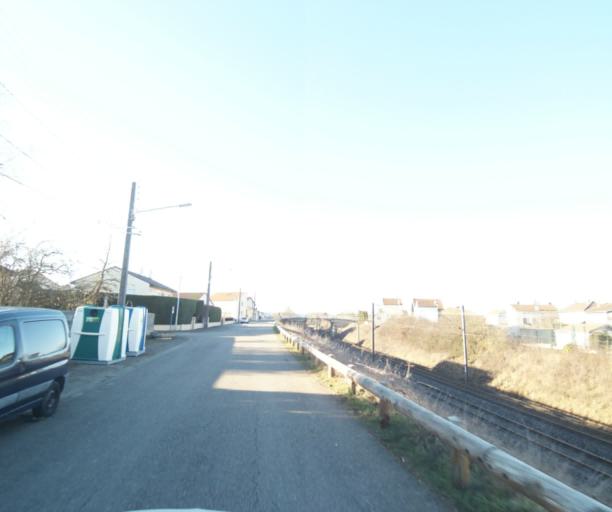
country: FR
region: Lorraine
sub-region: Departement de Meurthe-et-Moselle
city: Laneuveville-devant-Nancy
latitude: 48.6535
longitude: 6.2305
